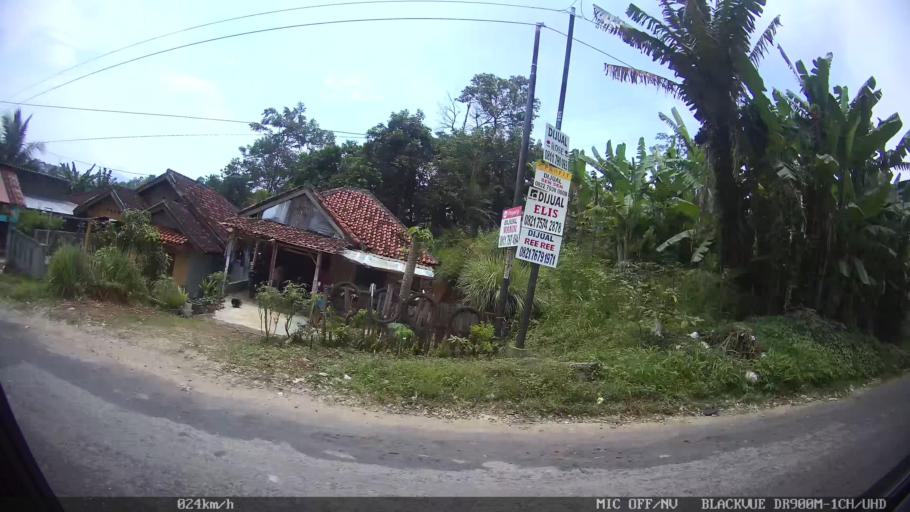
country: ID
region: Lampung
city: Bandarlampung
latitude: -5.4379
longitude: 105.2439
